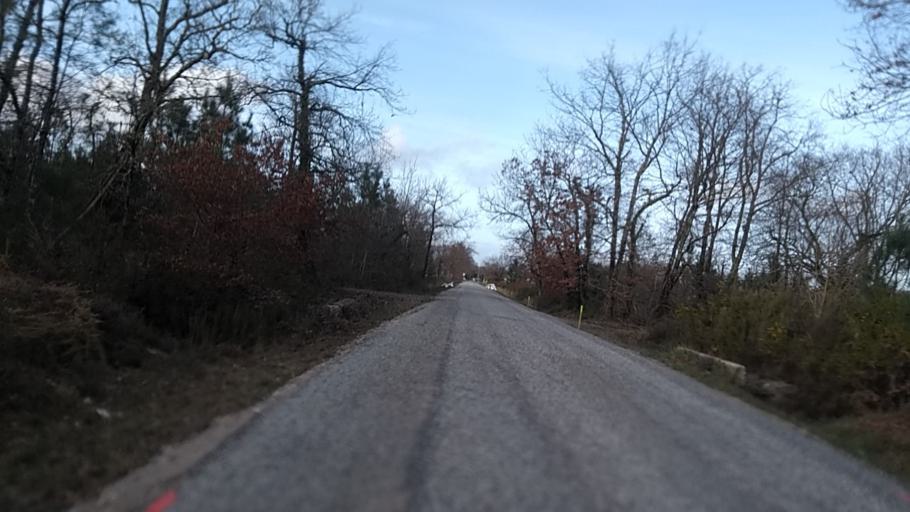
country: FR
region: Aquitaine
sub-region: Departement de la Gironde
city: Le Barp
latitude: 44.5922
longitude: -0.7687
